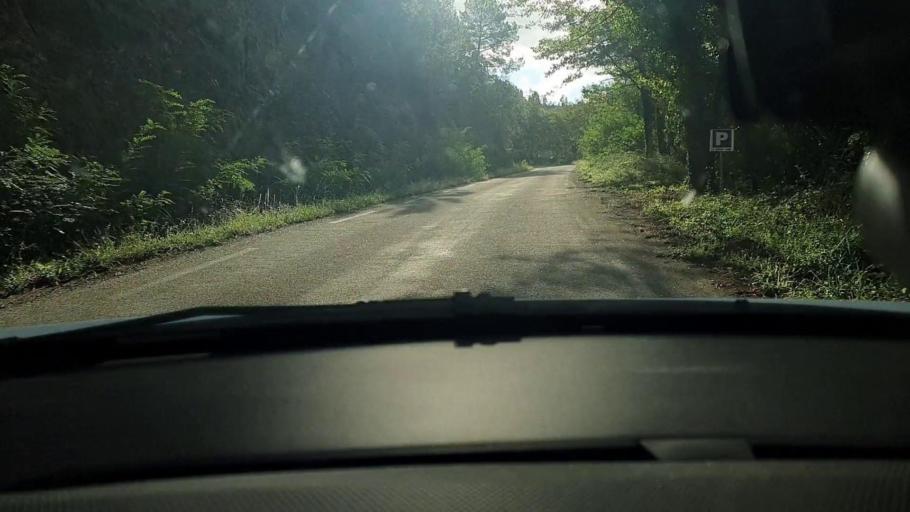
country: FR
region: Languedoc-Roussillon
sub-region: Departement du Gard
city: Besseges
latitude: 44.3201
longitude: 4.0387
